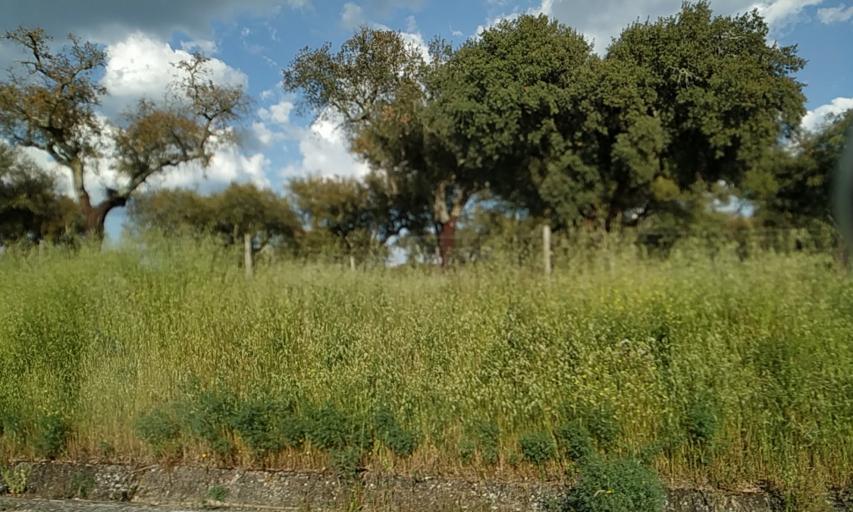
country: PT
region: Portalegre
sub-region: Portalegre
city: Urra
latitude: 39.2247
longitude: -7.4562
